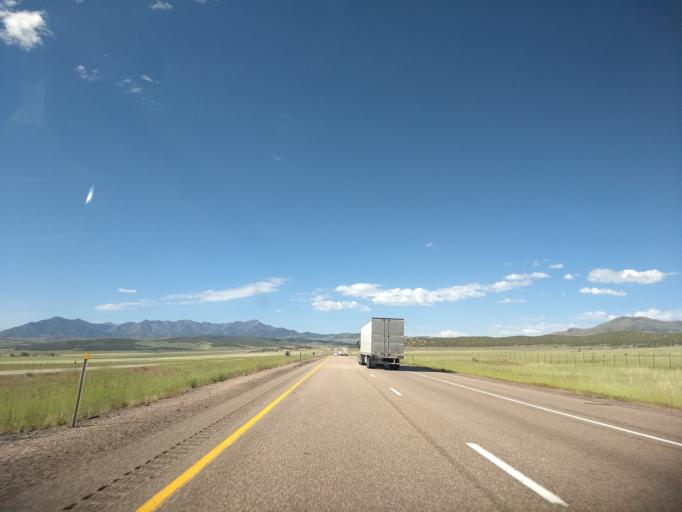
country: US
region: Utah
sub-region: Millard County
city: Fillmore
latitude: 39.1137
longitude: -112.2519
